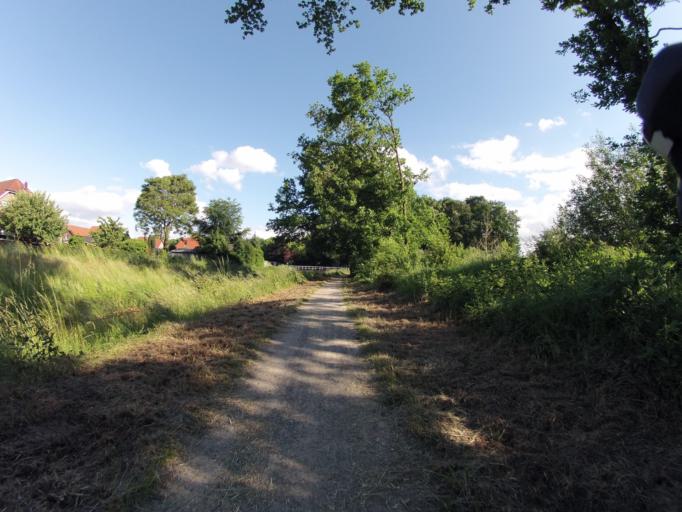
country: DE
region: North Rhine-Westphalia
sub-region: Regierungsbezirk Munster
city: Horstel
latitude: 52.2978
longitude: 7.5963
